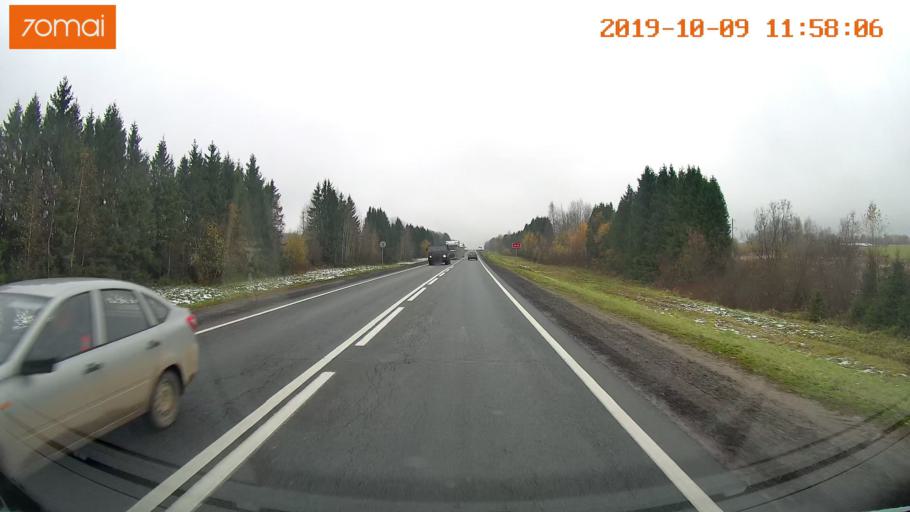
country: RU
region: Vologda
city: Gryazovets
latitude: 58.7230
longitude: 40.2960
